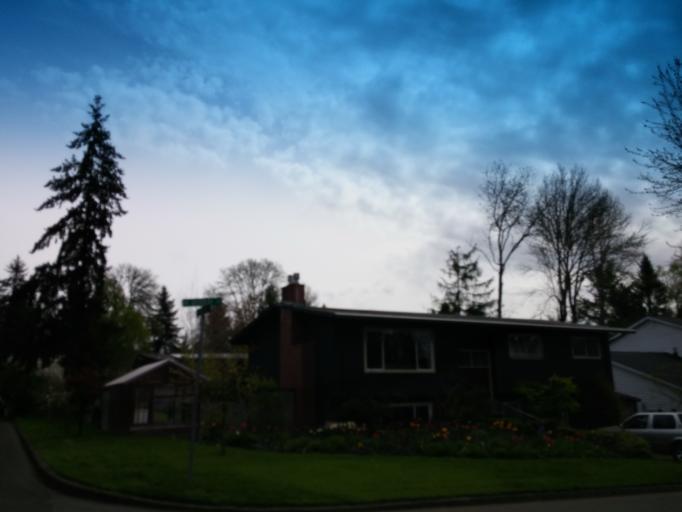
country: US
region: Oregon
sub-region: Washington County
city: Cedar Mill
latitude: 45.5325
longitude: -122.8130
